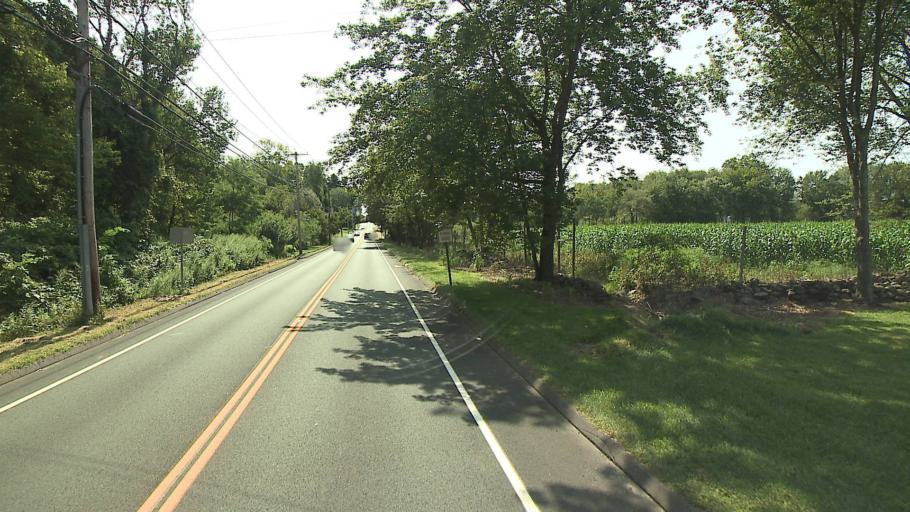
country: US
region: Connecticut
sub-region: Fairfield County
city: Trumbull
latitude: 41.2425
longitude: -73.2727
